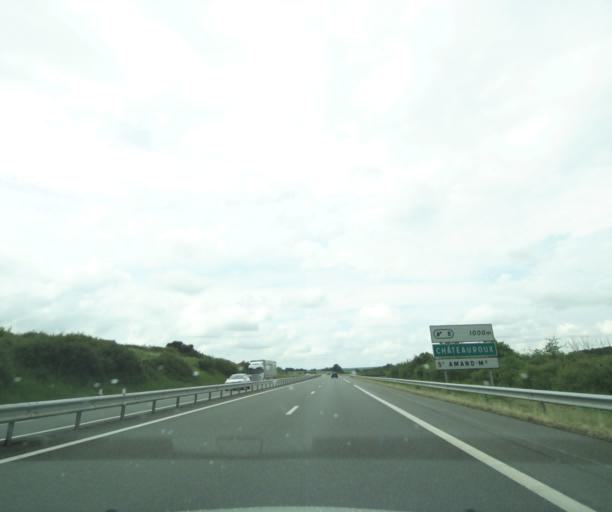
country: FR
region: Centre
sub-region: Departement du Cher
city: Orval
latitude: 46.7091
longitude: 2.4612
